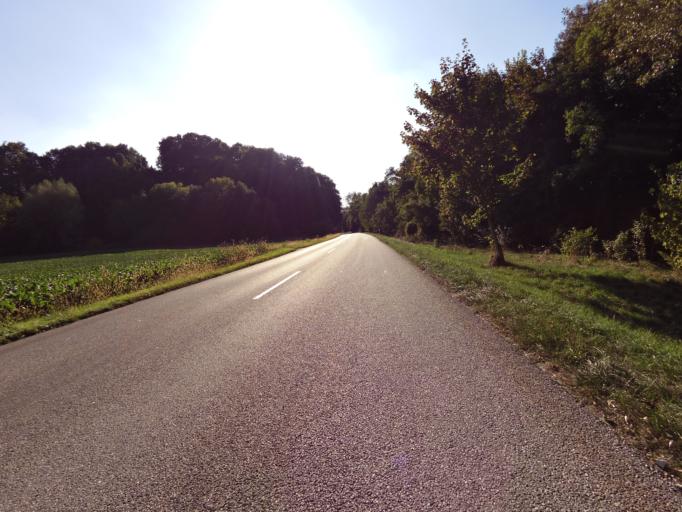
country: DE
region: Bavaria
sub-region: Lower Bavaria
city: Niederaichbach
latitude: 48.5945
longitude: 12.2891
